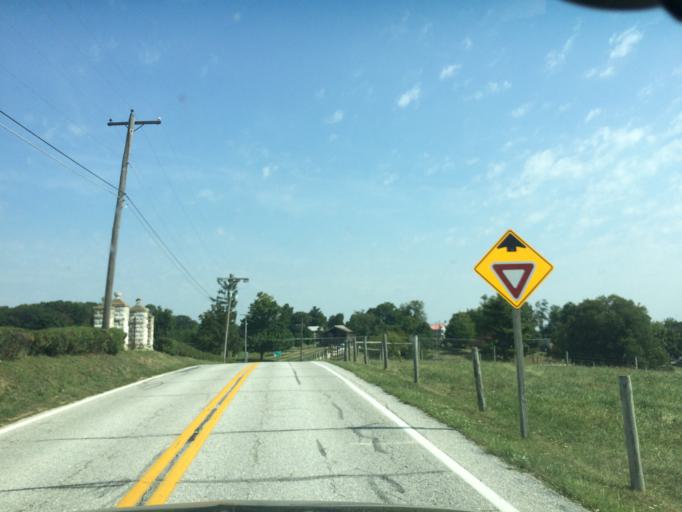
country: US
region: Maryland
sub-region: Carroll County
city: New Windsor
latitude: 39.5917
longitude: -77.1210
